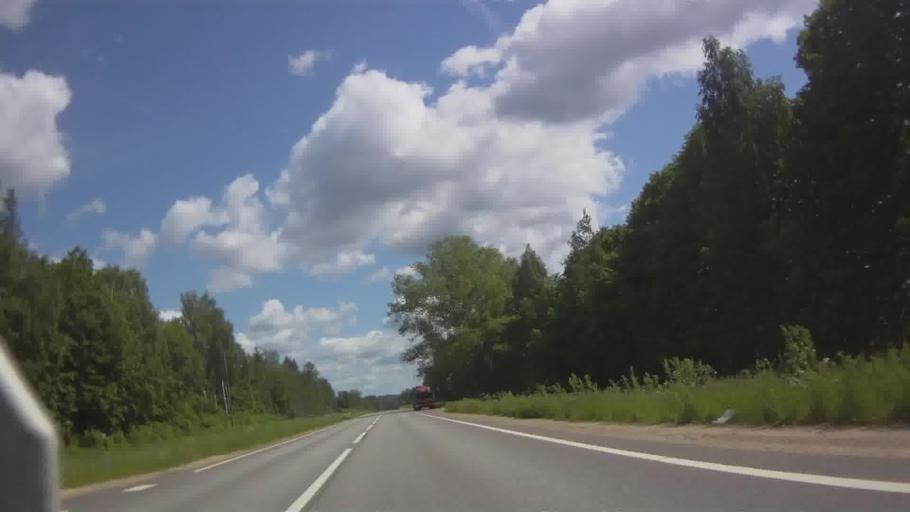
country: LV
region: Jekabpils Rajons
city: Jekabpils
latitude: 56.5297
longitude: 25.9970
